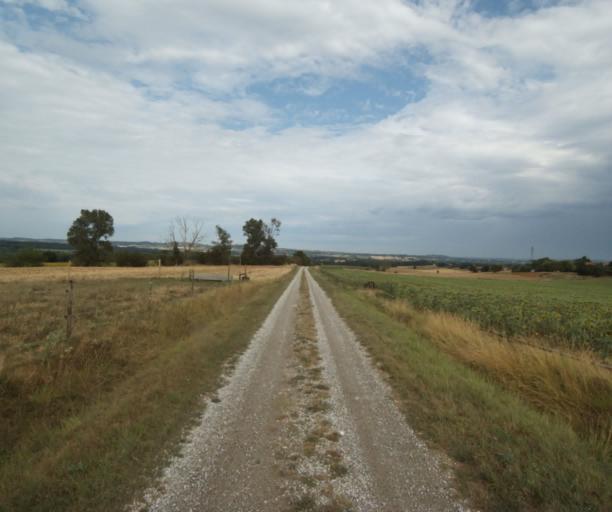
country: FR
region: Midi-Pyrenees
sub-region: Departement de la Haute-Garonne
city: Revel
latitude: 43.4264
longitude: 1.9687
